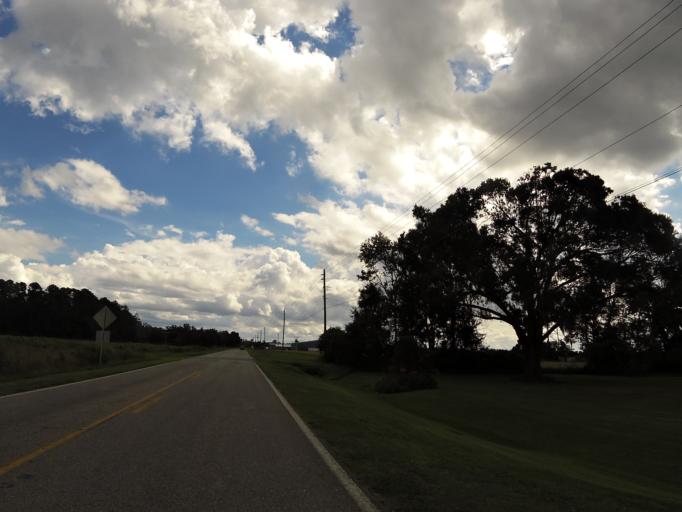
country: US
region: Florida
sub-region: Putnam County
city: East Palatka
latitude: 29.7624
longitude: -81.4756
